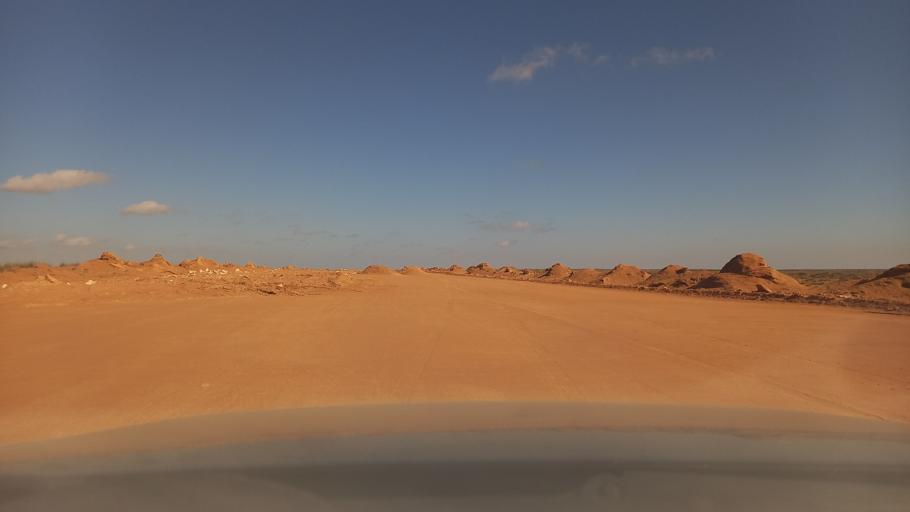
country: TN
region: Madanin
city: Medenine
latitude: 33.2363
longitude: 10.5515
